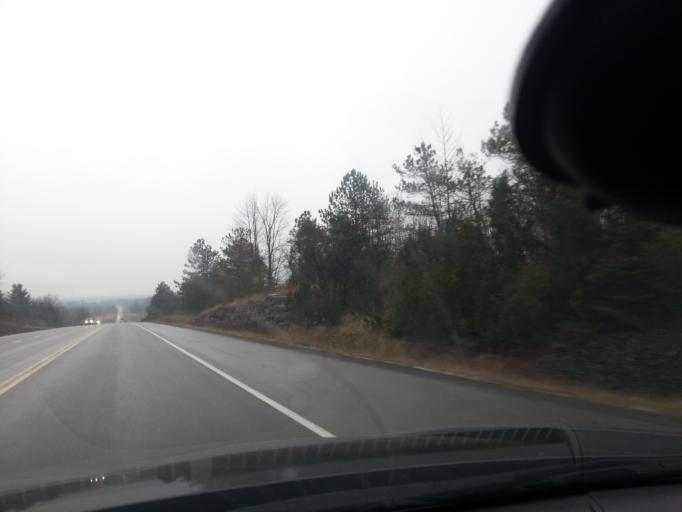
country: CA
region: Ontario
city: Quinte West
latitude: 44.4904
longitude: -77.6569
